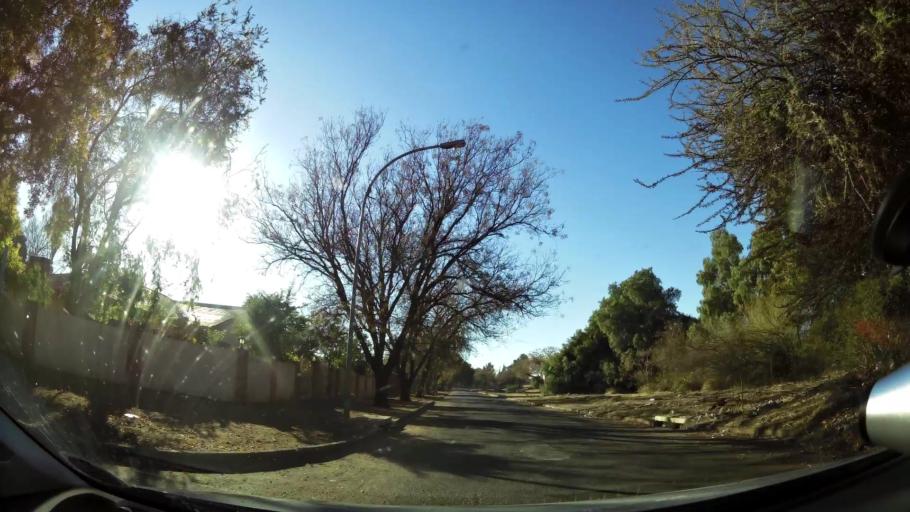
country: ZA
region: Northern Cape
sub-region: Frances Baard District Municipality
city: Kimberley
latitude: -28.7389
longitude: 24.7331
